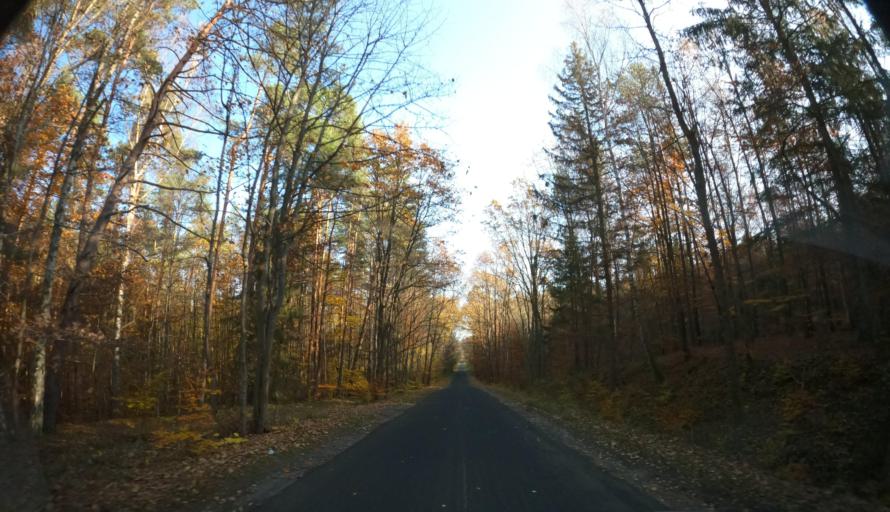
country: PL
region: West Pomeranian Voivodeship
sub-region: Powiat koszalinski
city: Polanow
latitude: 54.2408
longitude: 16.7181
